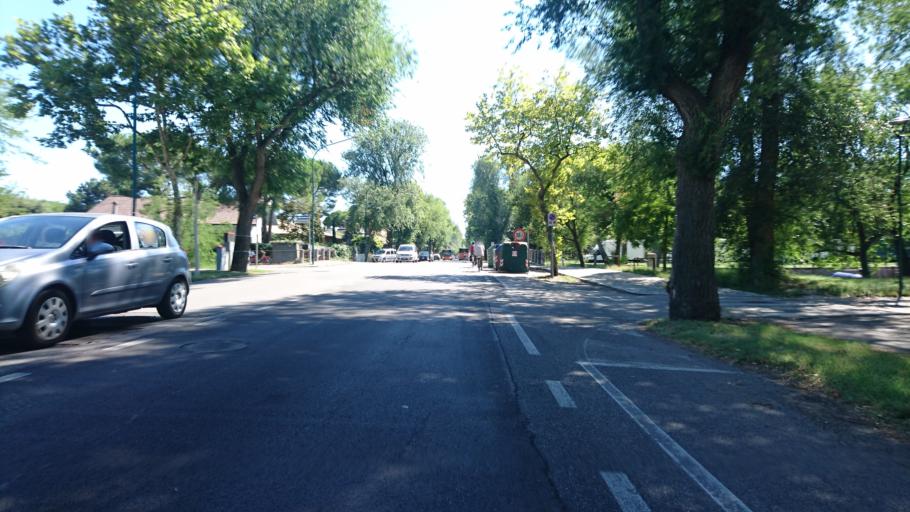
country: IT
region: Veneto
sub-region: Provincia di Venezia
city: Lido
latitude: 45.3964
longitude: 12.3571
